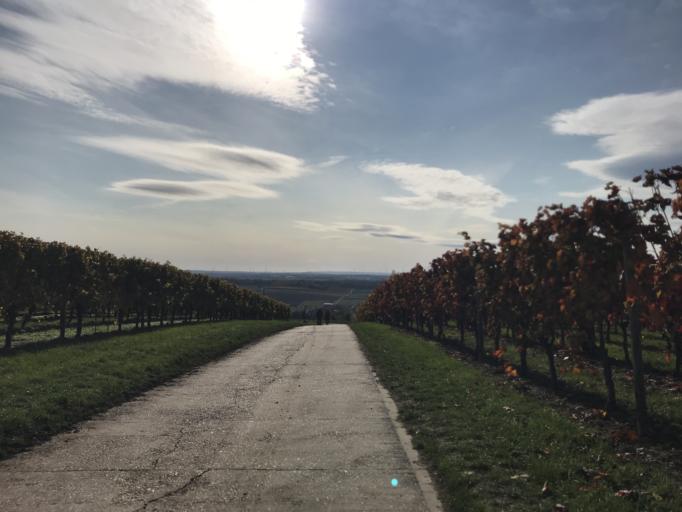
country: DE
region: Rheinland-Pfalz
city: Essenheim
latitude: 49.9227
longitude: 8.1502
